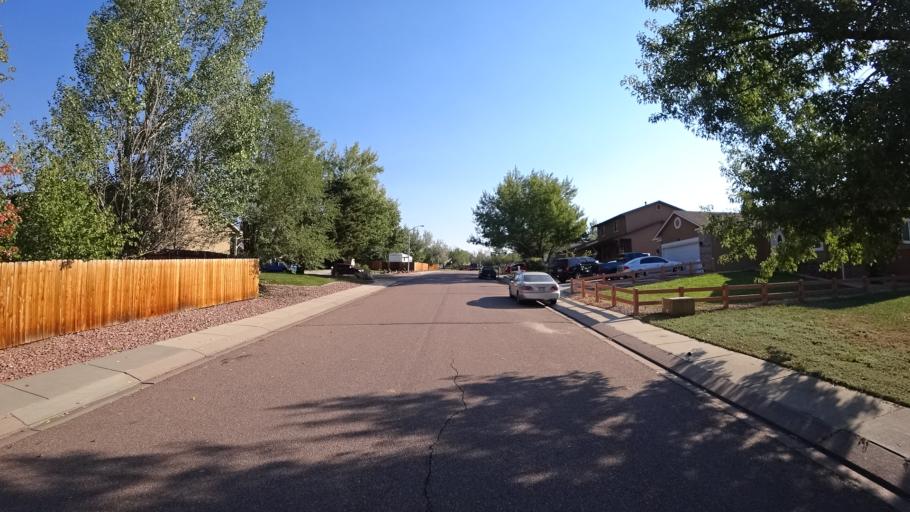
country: US
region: Colorado
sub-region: El Paso County
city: Stratmoor
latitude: 38.7758
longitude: -104.8018
